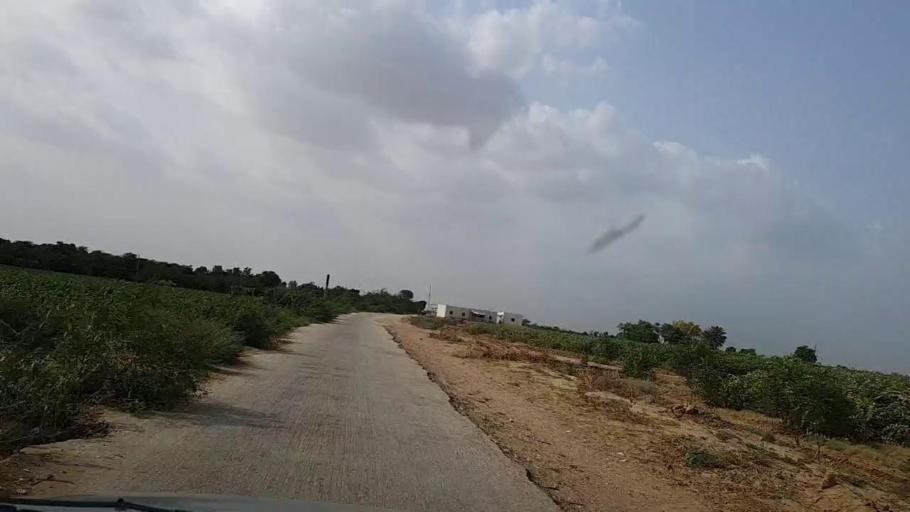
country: PK
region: Sindh
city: Kotri
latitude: 25.2544
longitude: 68.2569
